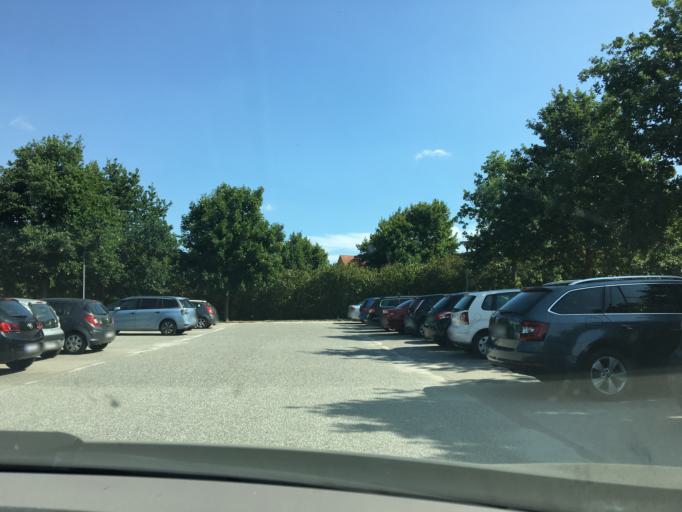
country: DK
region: South Denmark
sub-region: Odense Kommune
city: Odense
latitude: 55.3794
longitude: 10.3674
